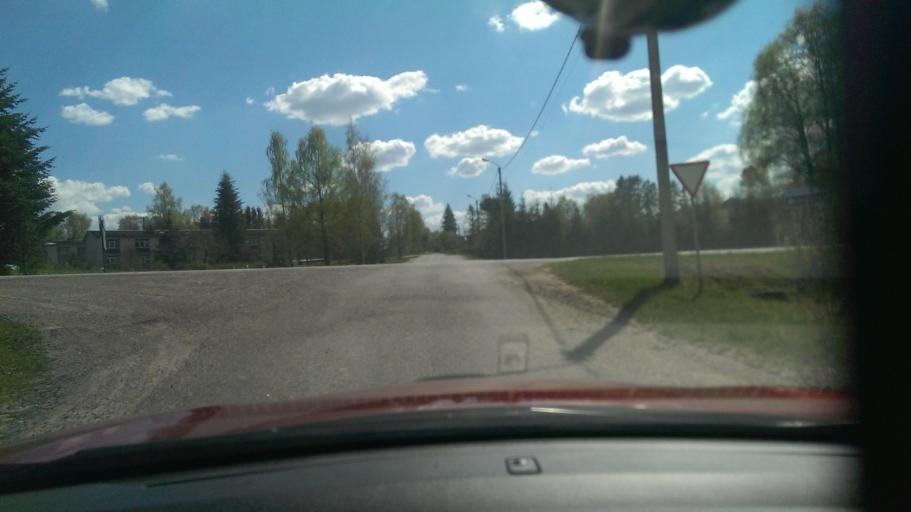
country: EE
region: Vorumaa
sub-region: Voru linn
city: Voru
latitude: 57.9831
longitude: 26.8768
